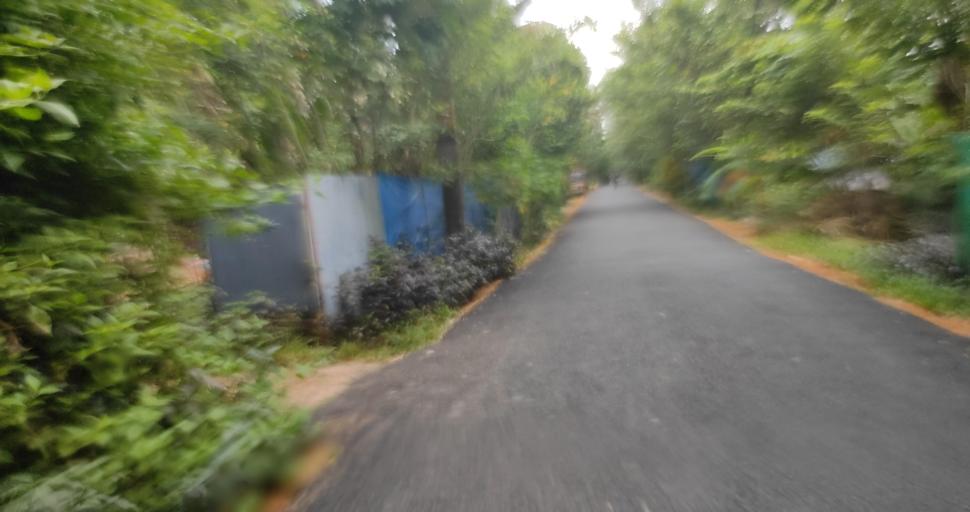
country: IN
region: Kerala
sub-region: Alappuzha
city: Shertallai
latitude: 9.6665
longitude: 76.3326
